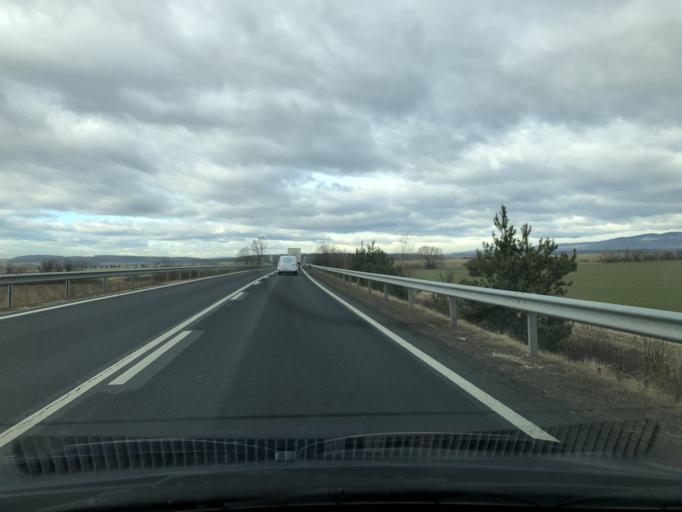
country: AT
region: Burgenland
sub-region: Politischer Bezirk Oberwart
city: Schachendorf
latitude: 47.2455
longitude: 16.5172
